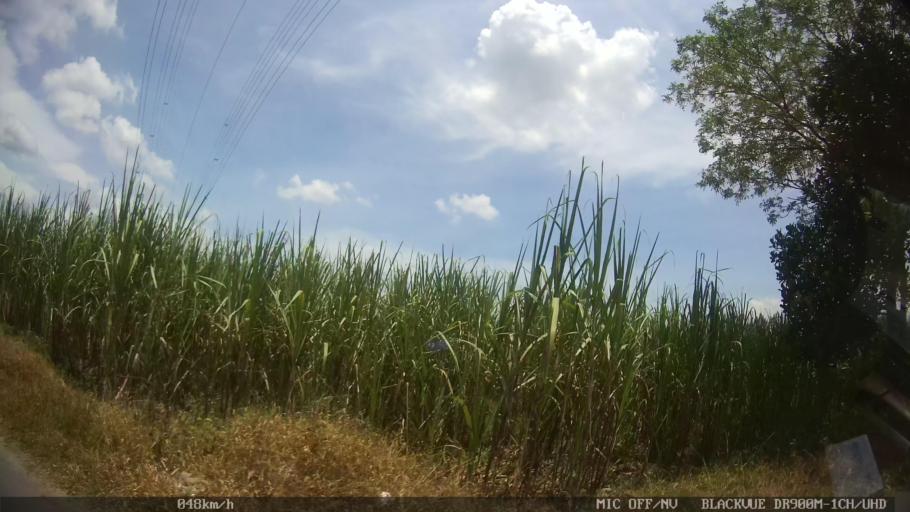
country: ID
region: North Sumatra
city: Binjai
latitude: 3.5913
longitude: 98.5304
